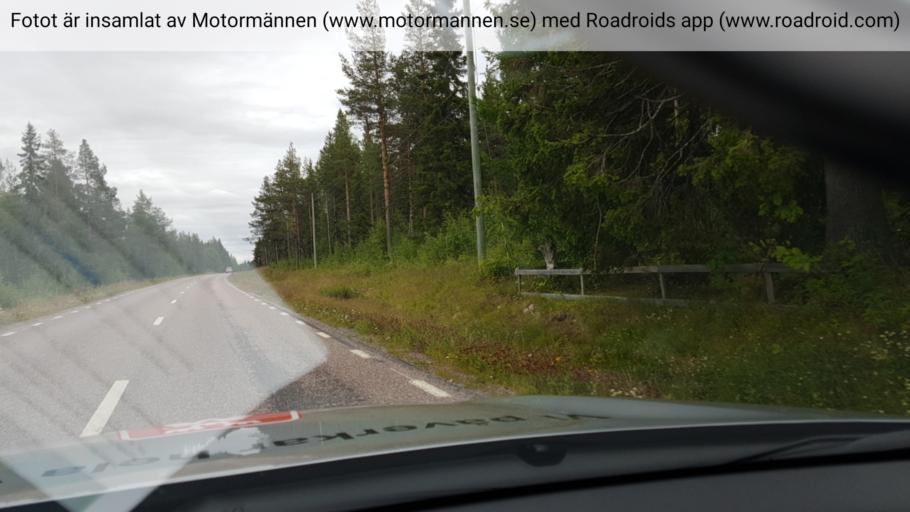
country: SE
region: Norrbotten
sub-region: Gallivare Kommun
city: Gaellivare
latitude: 67.0289
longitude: 21.7774
